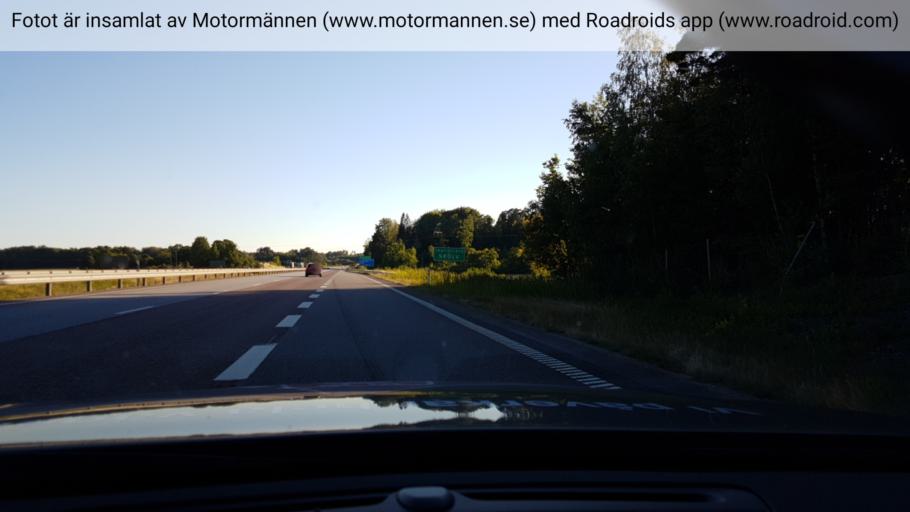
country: SE
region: OErebro
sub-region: Lindesbergs Kommun
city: Frovi
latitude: 59.3133
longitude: 15.4289
